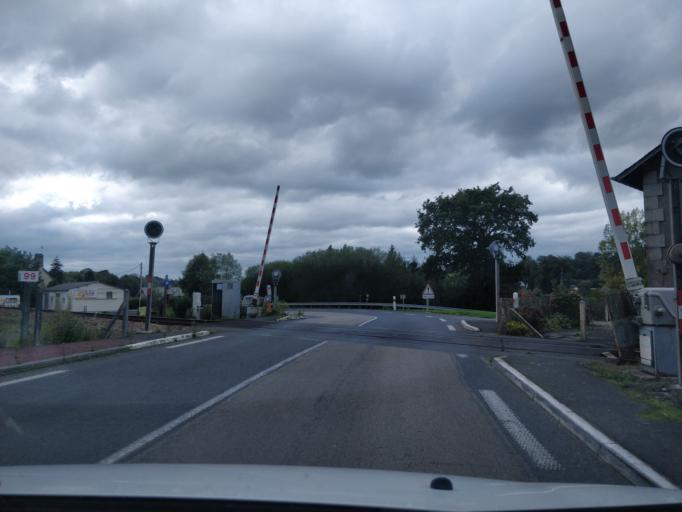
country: FR
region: Lower Normandy
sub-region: Departement de la Manche
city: Villedieu-les-Poeles
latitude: 48.8345
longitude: -1.1972
